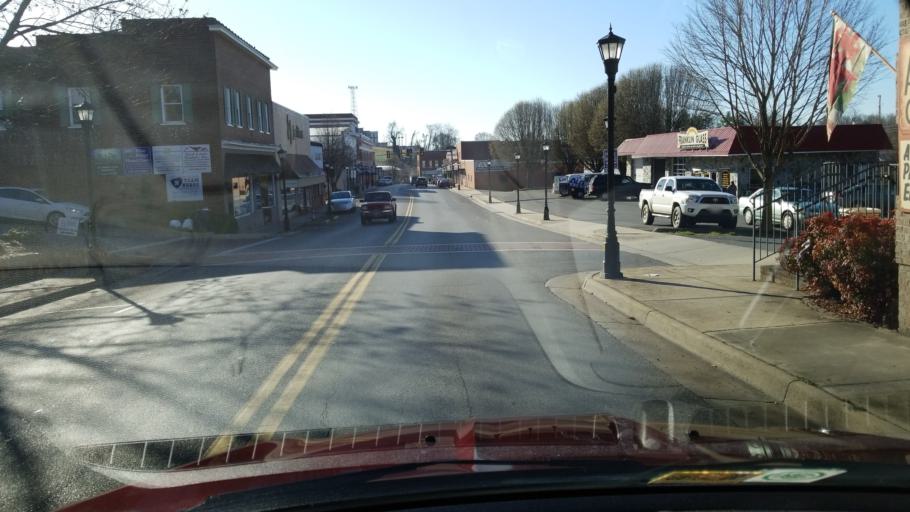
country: US
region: Virginia
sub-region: Franklin County
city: Rocky Mount
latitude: 36.9992
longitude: -79.8931
